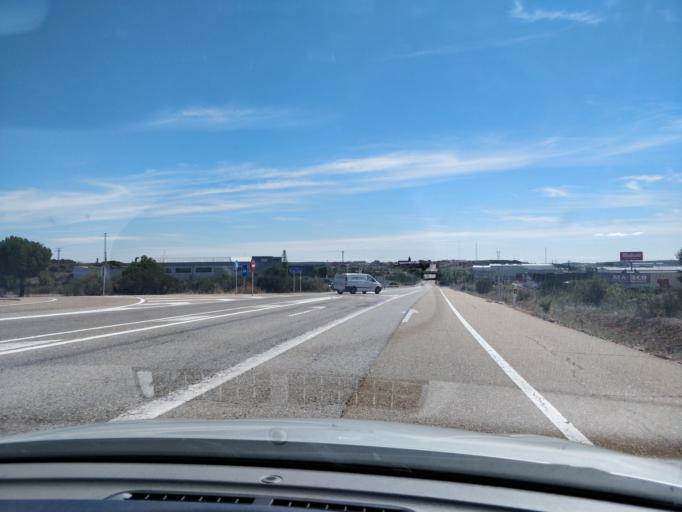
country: ES
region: Castille and Leon
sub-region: Provincia de Leon
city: Astorga
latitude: 42.4731
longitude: -6.0888
